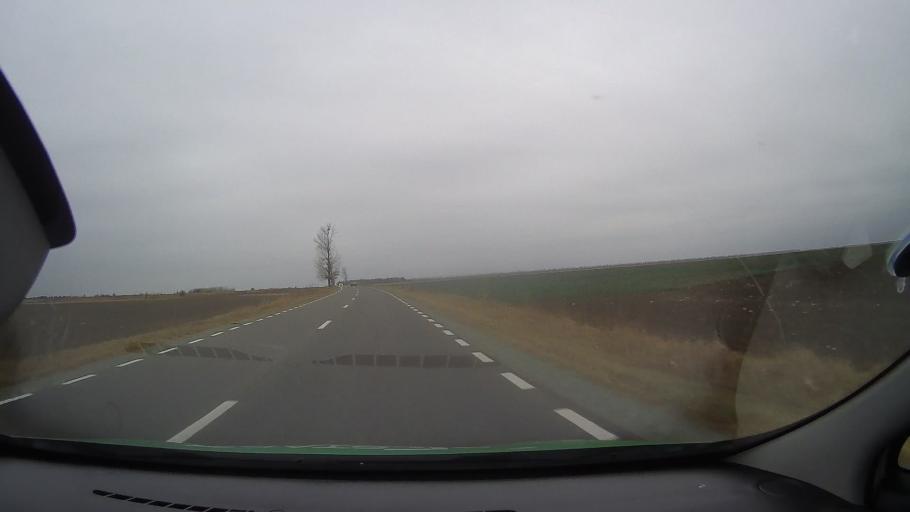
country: RO
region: Ialomita
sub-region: Comuna Scanteia
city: Iazu
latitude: 44.7146
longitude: 27.4194
